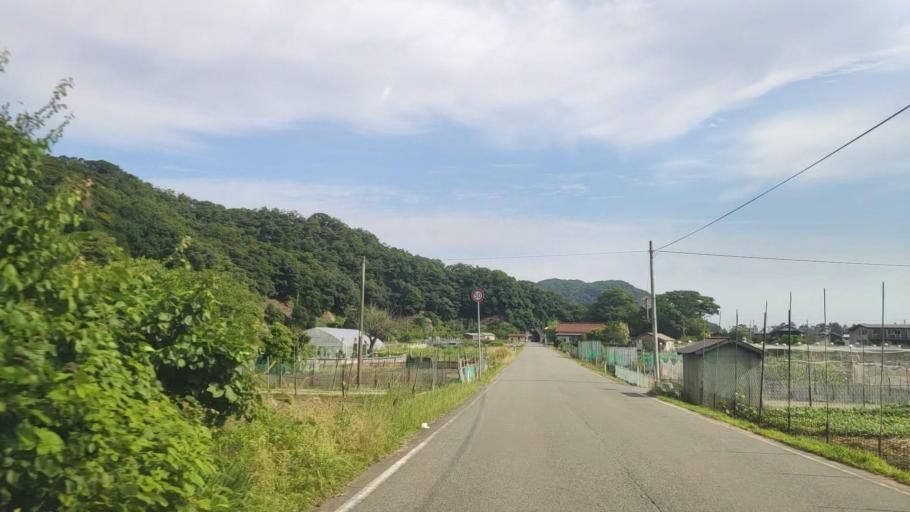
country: JP
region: Hyogo
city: Toyooka
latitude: 35.6365
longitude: 134.8365
